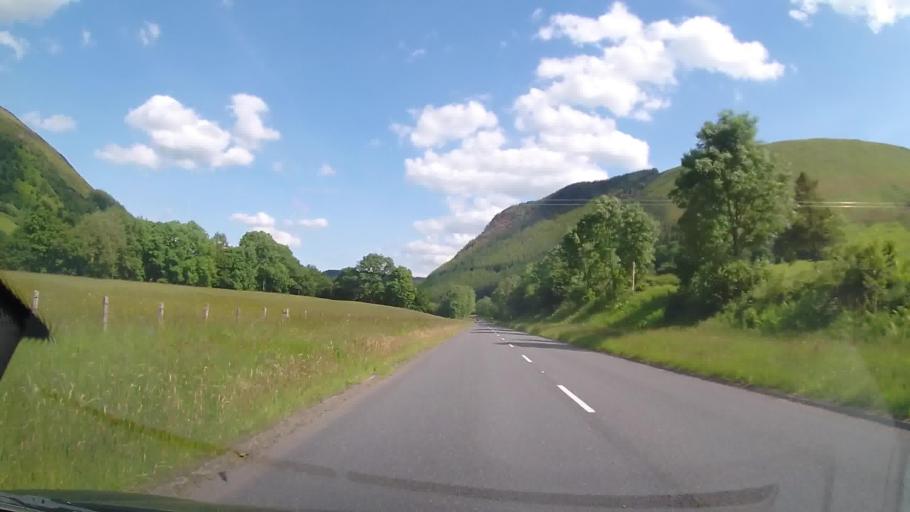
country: GB
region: Wales
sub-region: Gwynedd
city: Corris
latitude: 52.7278
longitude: -3.7123
